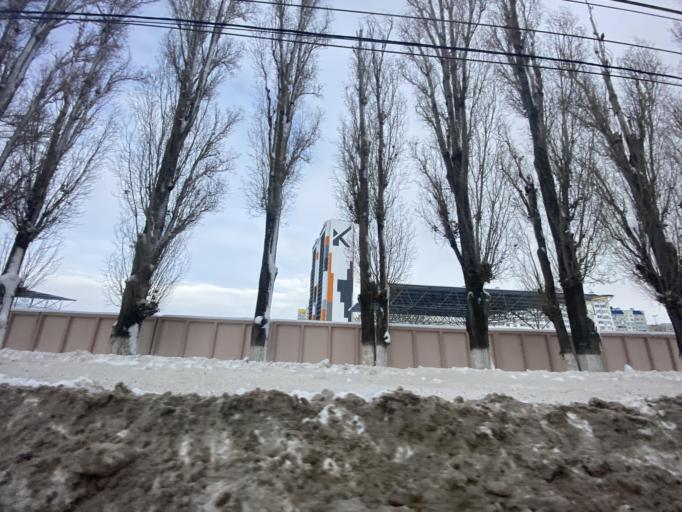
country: RU
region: Saratov
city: Engel's
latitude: 51.4990
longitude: 46.0871
